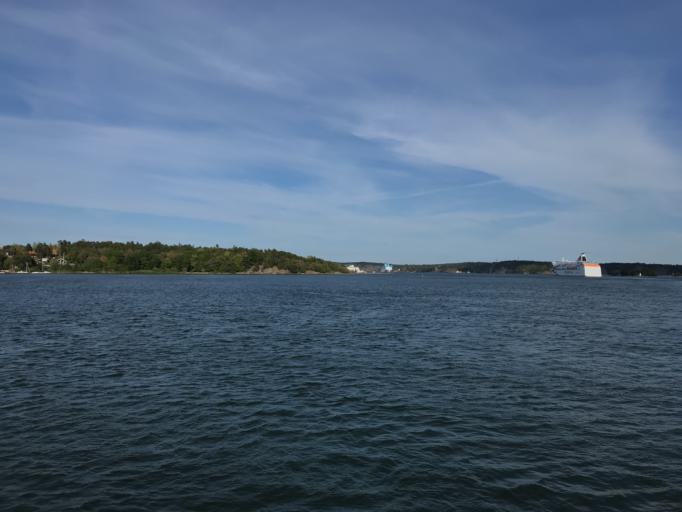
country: SE
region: Stockholm
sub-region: Nacka Kommun
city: Nacka
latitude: 59.3395
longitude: 18.1526
